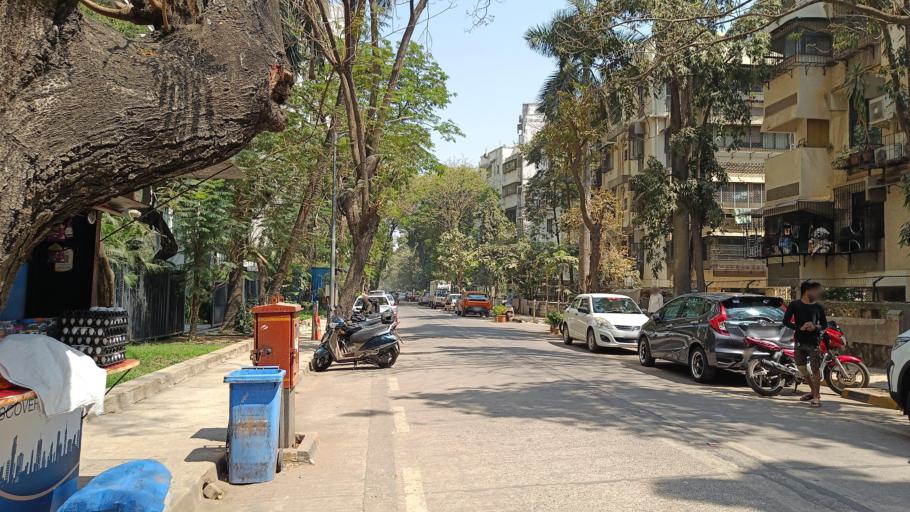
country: IN
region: Maharashtra
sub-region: Mumbai Suburban
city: Mumbai
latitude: 19.0566
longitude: 72.8501
